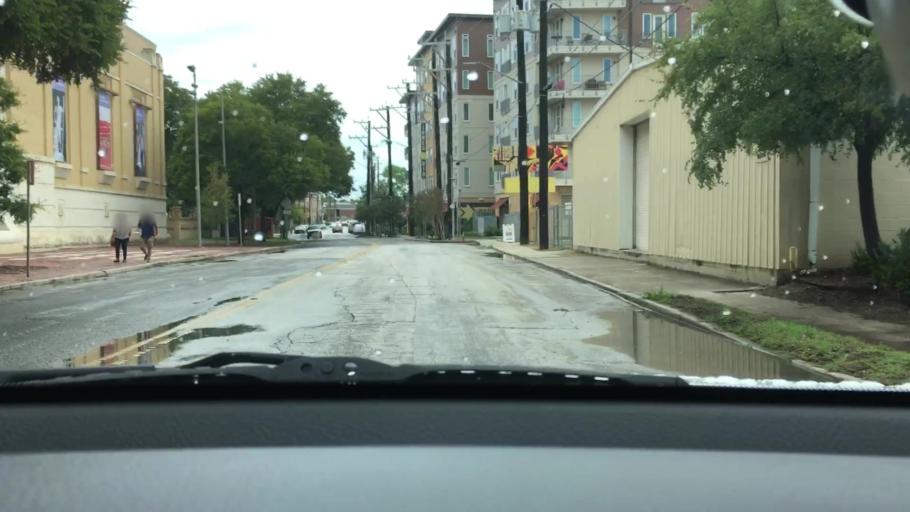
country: US
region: Texas
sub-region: Bexar County
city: San Antonio
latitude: 29.4370
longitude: -98.4822
